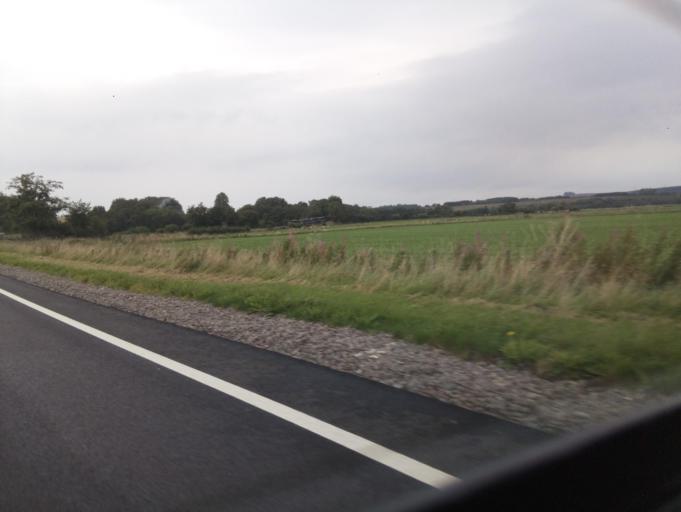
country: GB
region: Scotland
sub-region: Dumfries and Galloway
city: Locharbriggs
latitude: 55.1673
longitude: -3.5493
